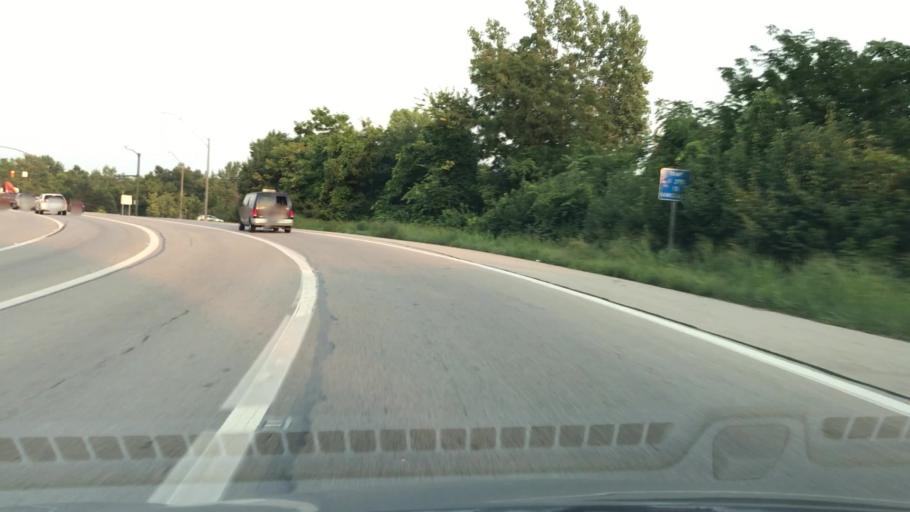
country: US
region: Ohio
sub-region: Franklin County
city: Gahanna
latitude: 40.0032
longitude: -82.8697
